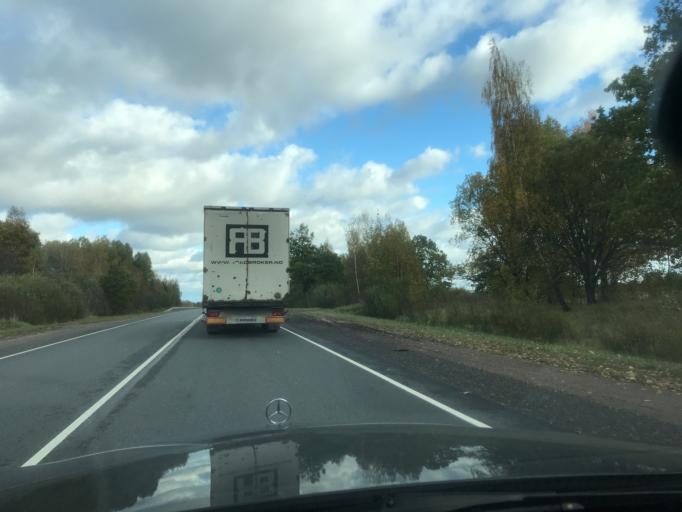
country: RU
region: Pskov
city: Novosokol'niki
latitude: 56.3447
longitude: 29.9413
